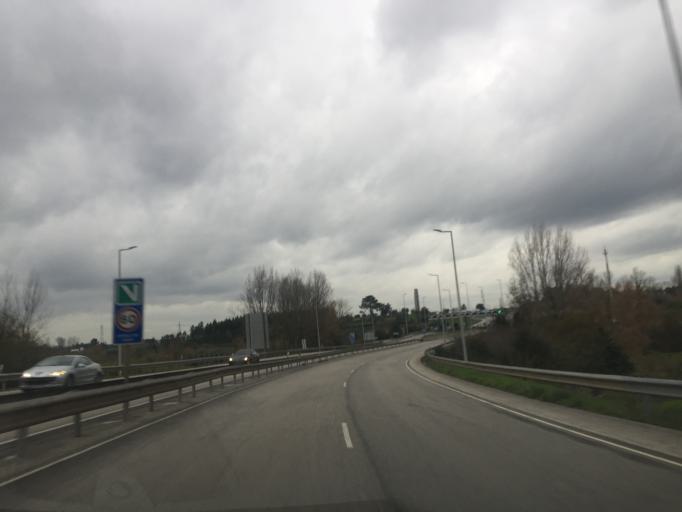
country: PT
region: Coimbra
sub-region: Condeixa-A-Nova
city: Condeixa-a-Nova
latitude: 40.1298
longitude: -8.4897
